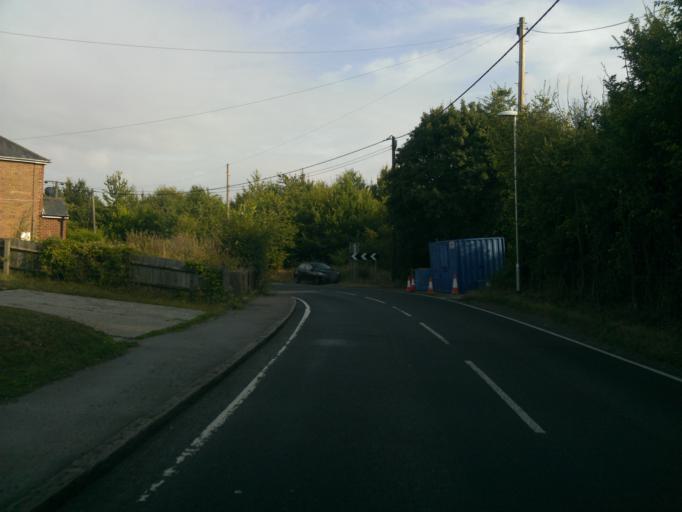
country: GB
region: England
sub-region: Essex
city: Witham
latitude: 51.8195
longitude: 0.6594
